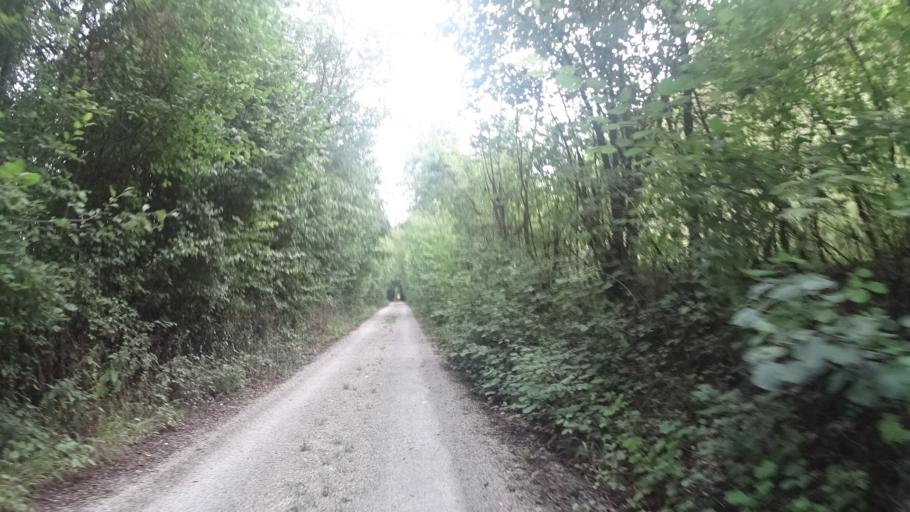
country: FR
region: Picardie
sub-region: Departement de l'Aisne
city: Origny-Sainte-Benoite
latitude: 49.8618
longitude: 3.5131
